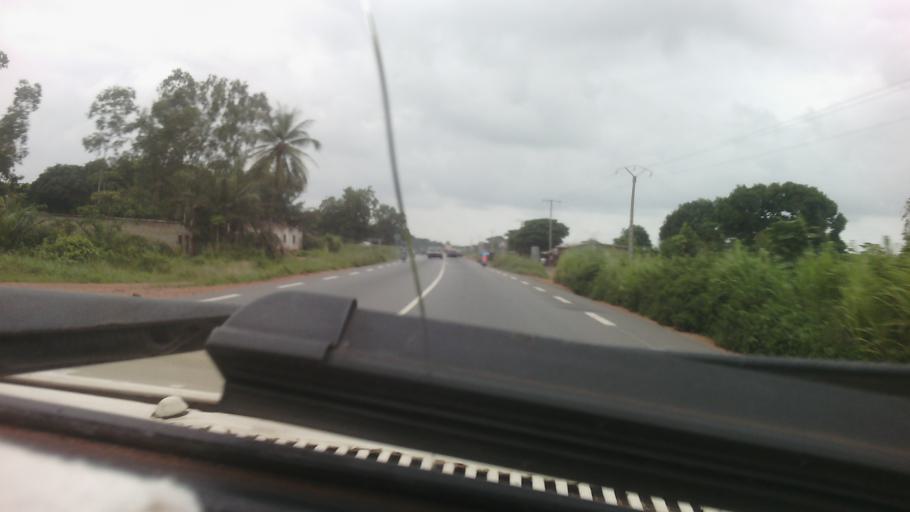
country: BJ
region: Atlantique
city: Ouidah
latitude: 6.3864
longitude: 2.0076
